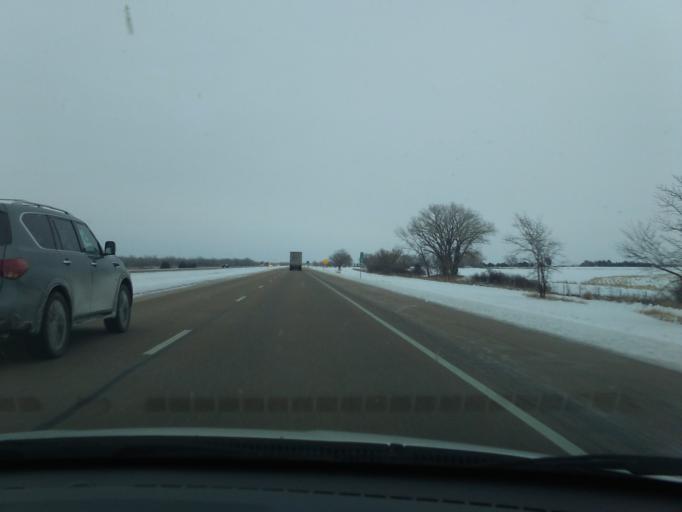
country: US
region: Nebraska
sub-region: Keith County
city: Ogallala
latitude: 41.1050
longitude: -101.7648
